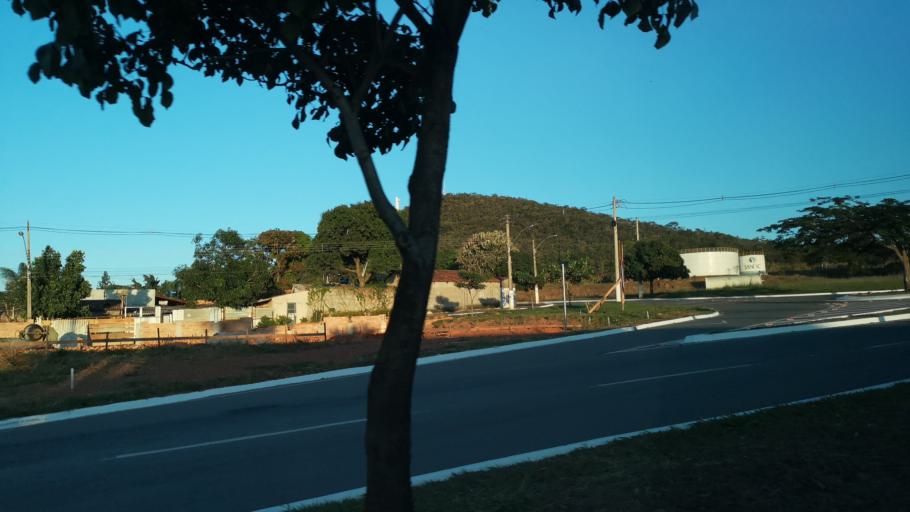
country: BR
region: Goias
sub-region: Senador Canedo
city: Senador Canedo
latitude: -16.6826
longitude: -49.1165
